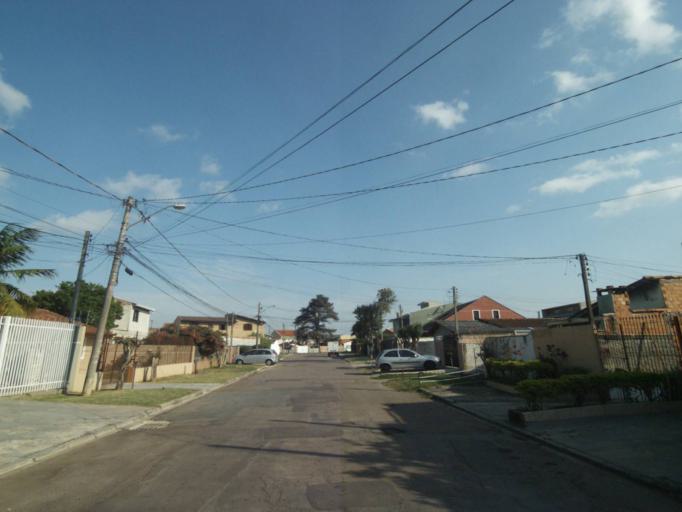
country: BR
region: Parana
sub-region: Curitiba
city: Curitiba
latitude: -25.4811
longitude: -49.3328
